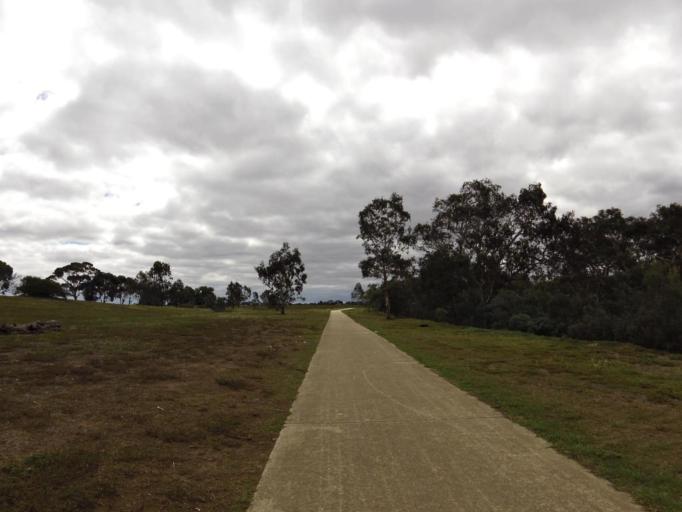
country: AU
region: Victoria
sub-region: Wyndham
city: Werribee
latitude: -37.8851
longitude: 144.6405
